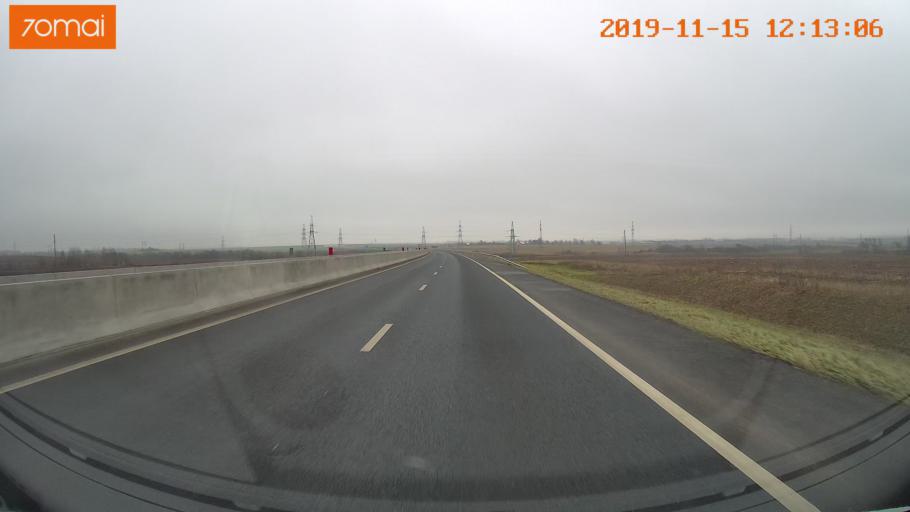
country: RU
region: Vologda
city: Vologda
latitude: 59.1678
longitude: 39.7789
